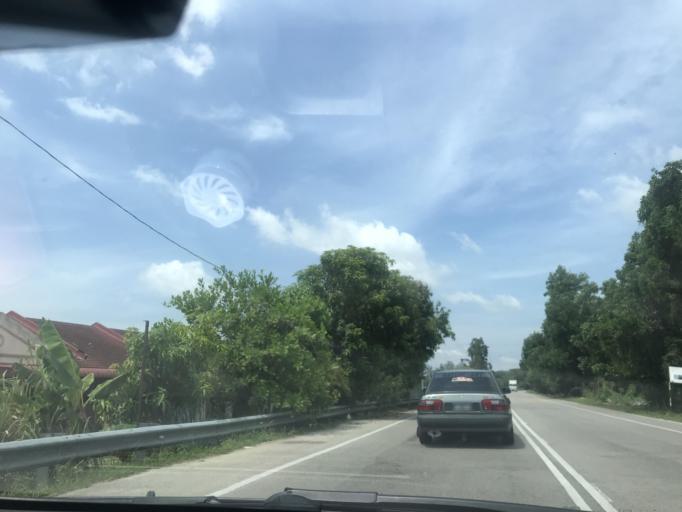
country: MY
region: Kelantan
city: Tumpat
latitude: 6.1980
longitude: 102.1555
